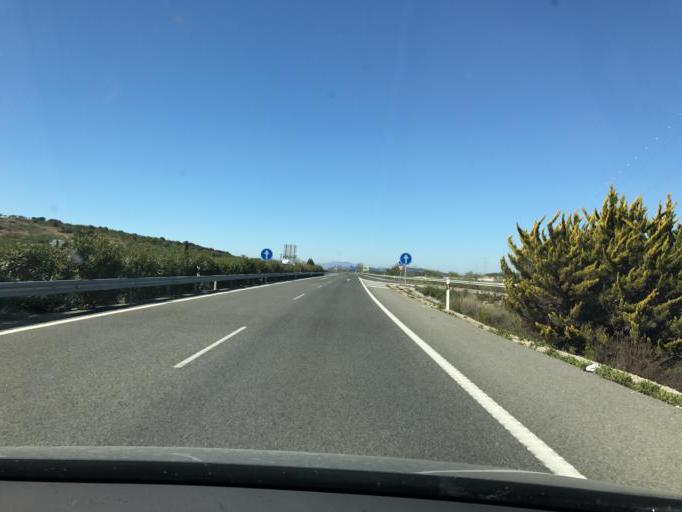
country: ES
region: Andalusia
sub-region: Provincia de Malaga
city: Villanueva de Tapia
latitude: 37.1179
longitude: -4.2976
